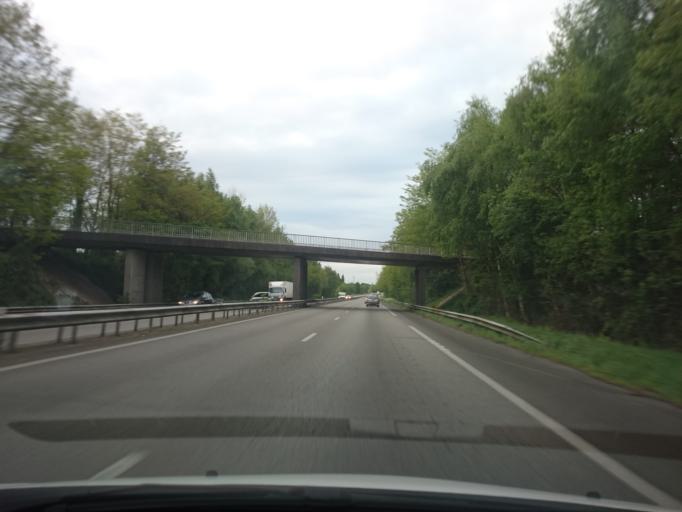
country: FR
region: Pays de la Loire
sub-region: Departement de la Loire-Atlantique
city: Treillieres
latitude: 47.3535
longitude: -1.6560
